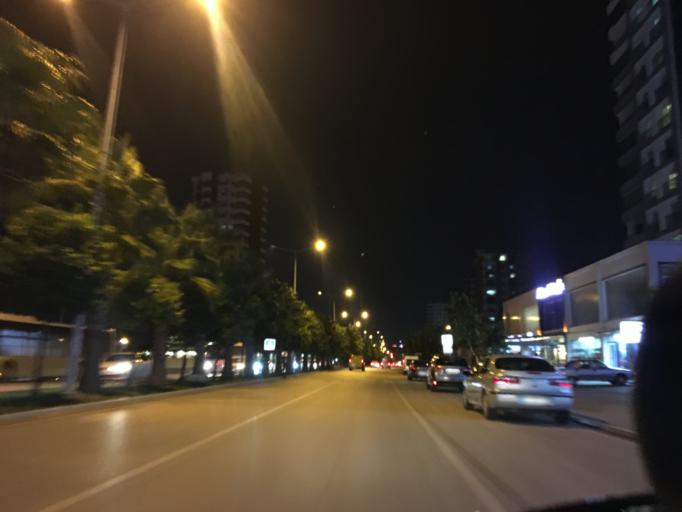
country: TR
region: Adana
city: Seyhan
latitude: 37.0220
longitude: 35.2771
